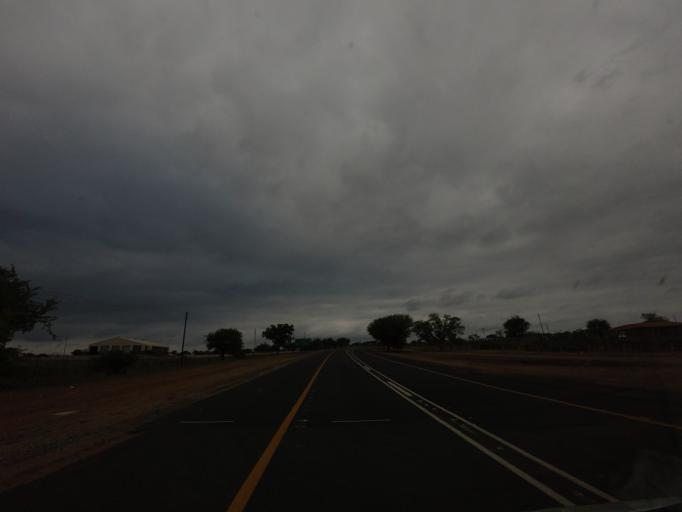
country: ZA
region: Mpumalanga
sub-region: Ehlanzeni District
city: Komatipoort
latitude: -25.4450
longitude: 31.6763
